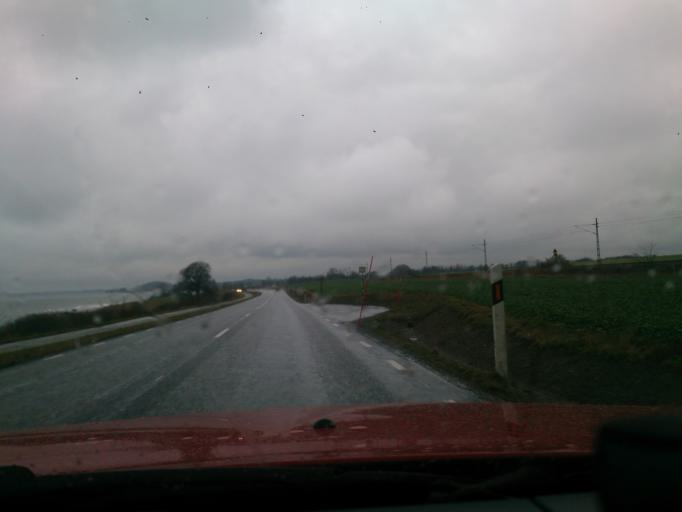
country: SE
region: Skane
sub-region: Ystads Kommun
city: Ystad
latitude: 55.4268
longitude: 13.7392
